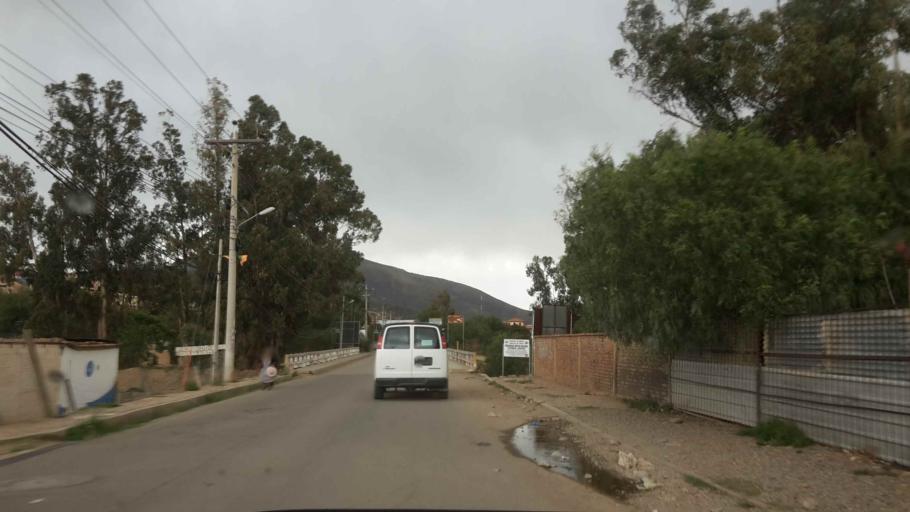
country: BO
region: Cochabamba
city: Tarata
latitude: -17.6094
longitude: -66.0248
